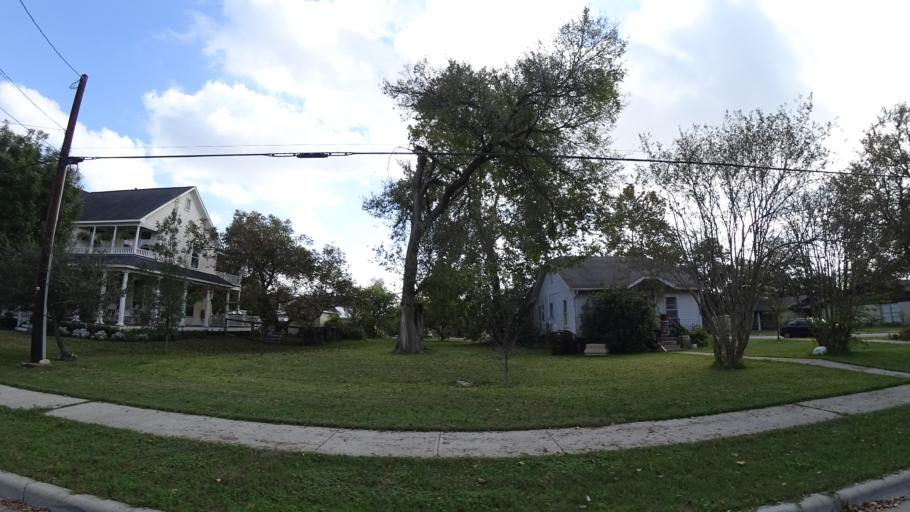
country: US
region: Texas
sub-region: Williamson County
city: Round Rock
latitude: 30.5119
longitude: -97.6705
